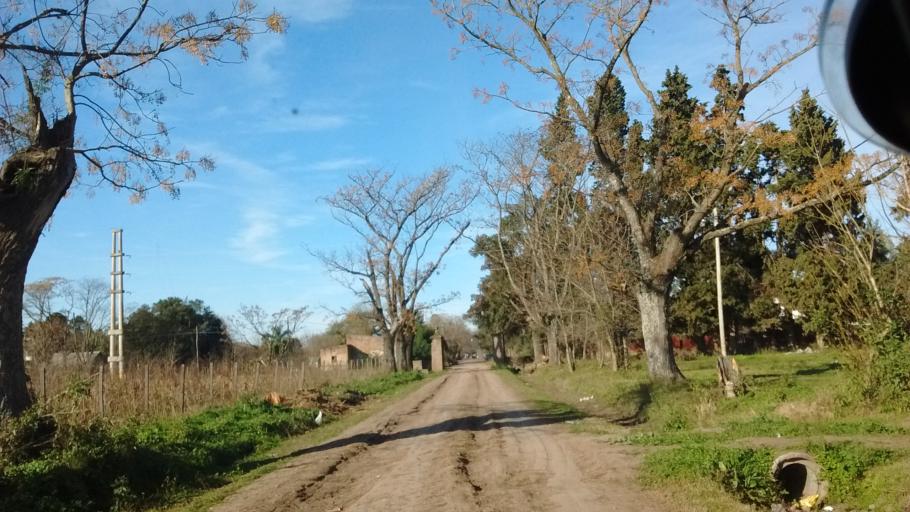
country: AR
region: Santa Fe
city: Funes
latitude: -32.9110
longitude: -60.8169
